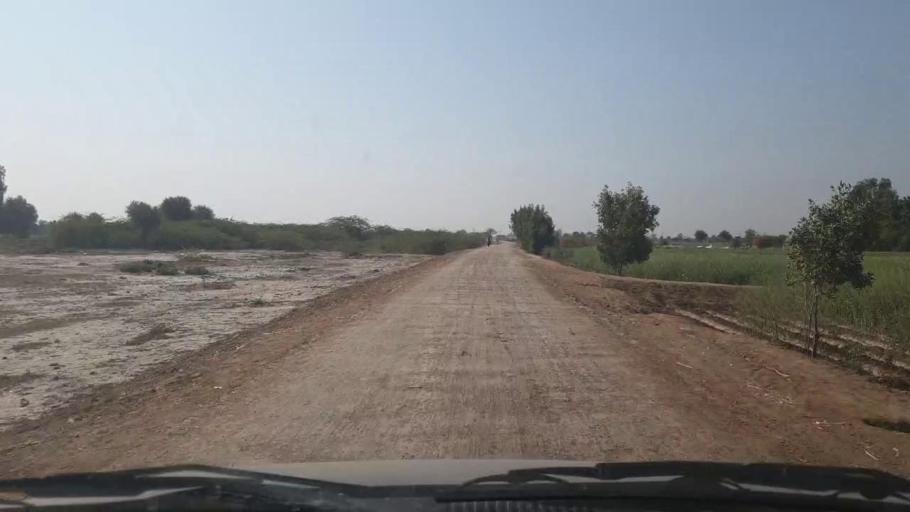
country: PK
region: Sindh
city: Samaro
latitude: 25.2853
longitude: 69.2970
